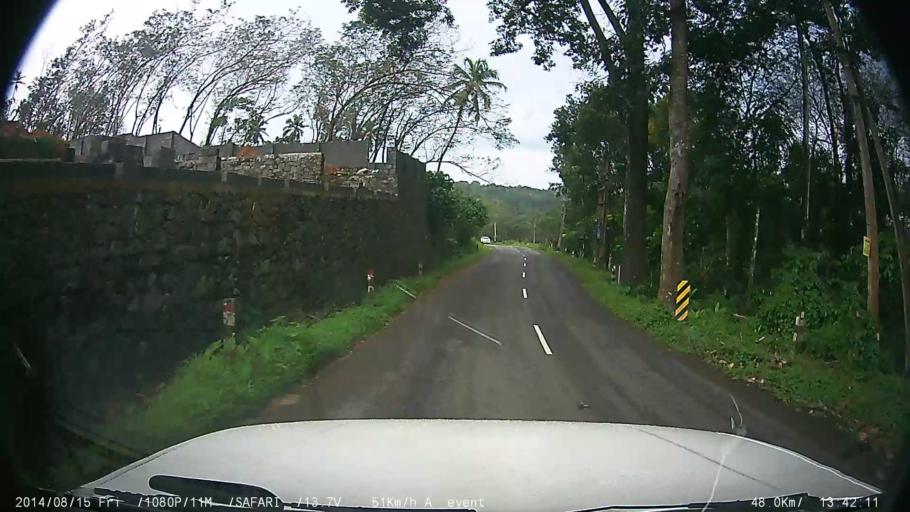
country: IN
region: Kerala
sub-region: Kottayam
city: Palackattumala
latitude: 9.7596
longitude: 76.5824
